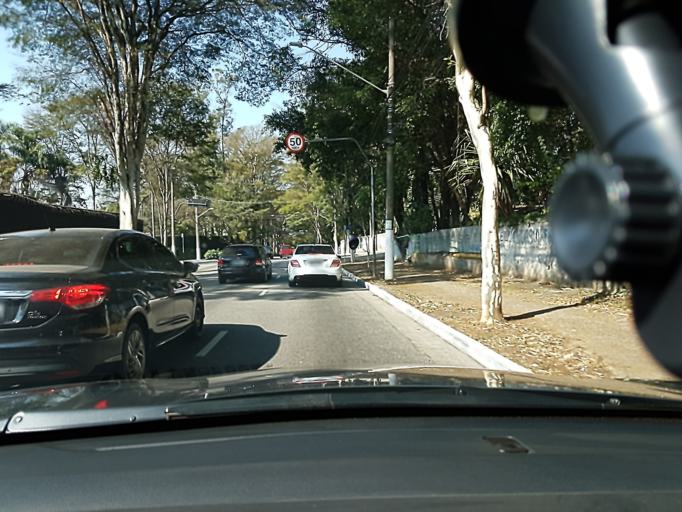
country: BR
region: Sao Paulo
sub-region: Taboao Da Serra
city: Taboao da Serra
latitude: -23.6170
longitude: -46.7101
